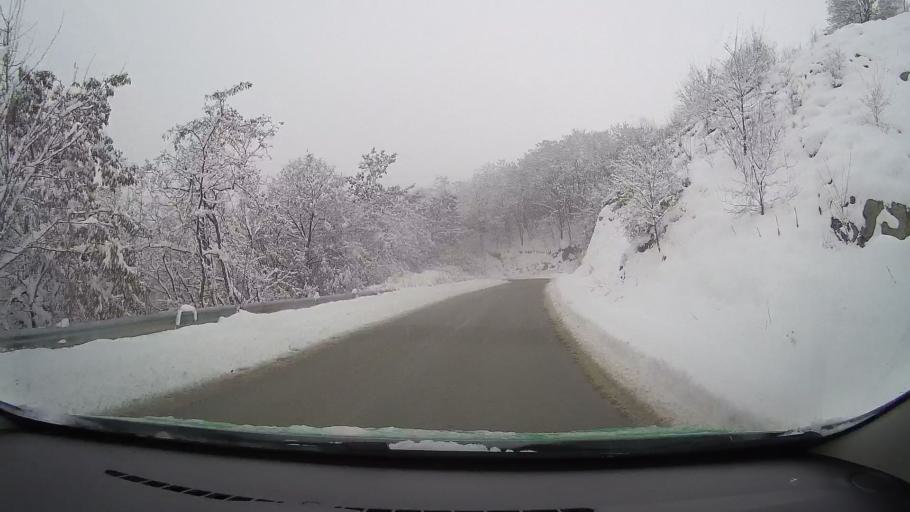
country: RO
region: Sibiu
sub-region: Comuna Jina
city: Jina
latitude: 45.7713
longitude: 23.6651
